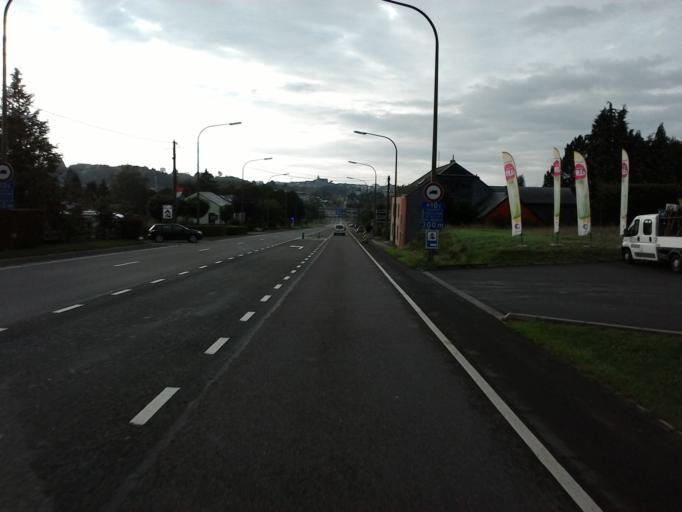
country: BE
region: Wallonia
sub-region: Province du Luxembourg
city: Arlon
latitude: 49.7028
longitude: 5.8062
